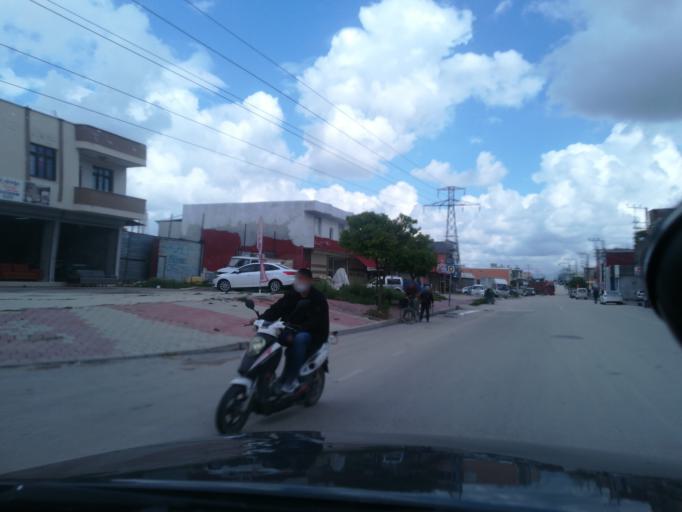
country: TR
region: Adana
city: Yuregir
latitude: 36.9764
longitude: 35.3876
